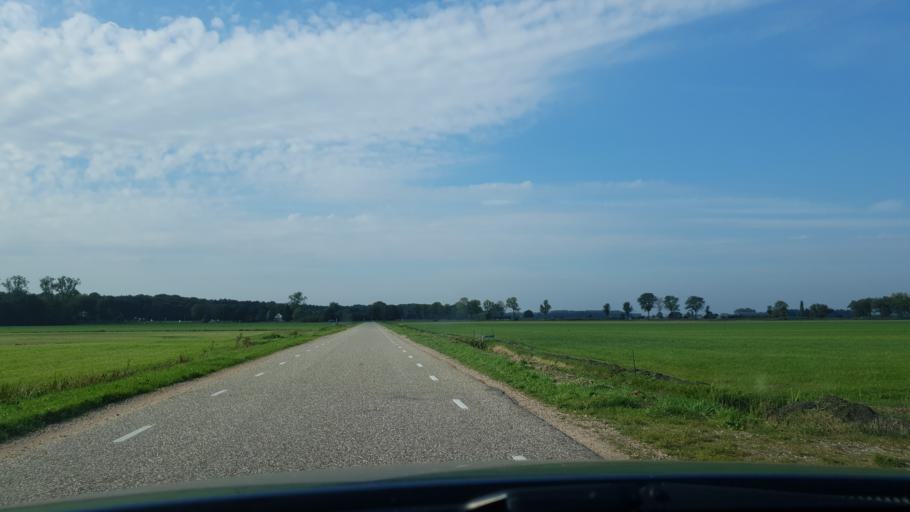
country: NL
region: Gelderland
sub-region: Gemeente Wijchen
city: Bergharen
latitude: 51.8540
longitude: 5.6869
